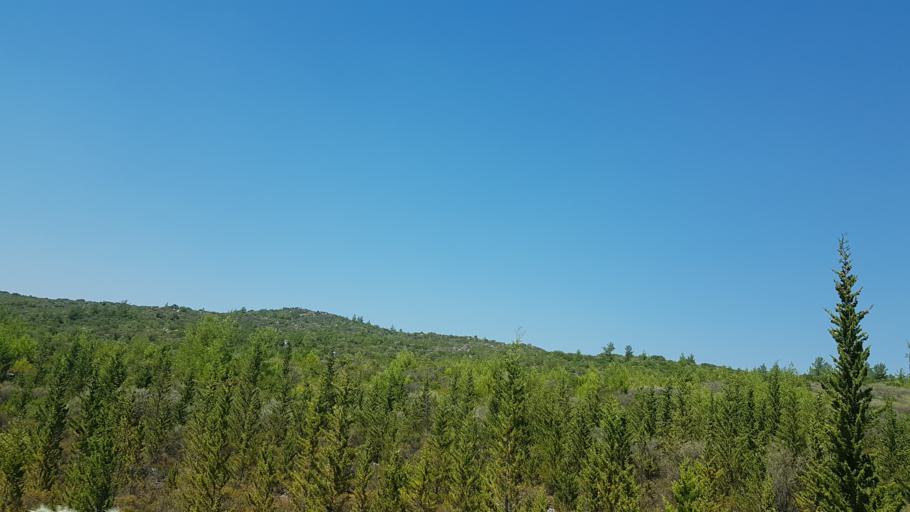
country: TR
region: Mugla
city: Karaova
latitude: 37.0462
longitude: 27.6999
